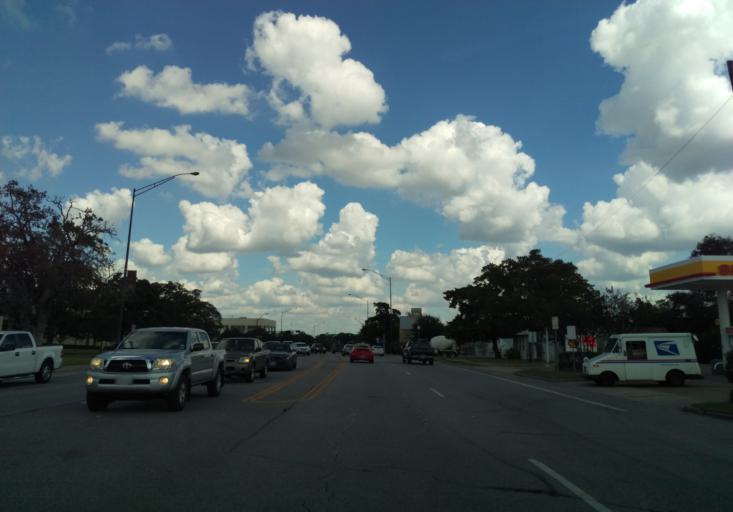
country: US
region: Texas
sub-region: Brazos County
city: College Station
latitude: 30.6061
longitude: -96.3375
